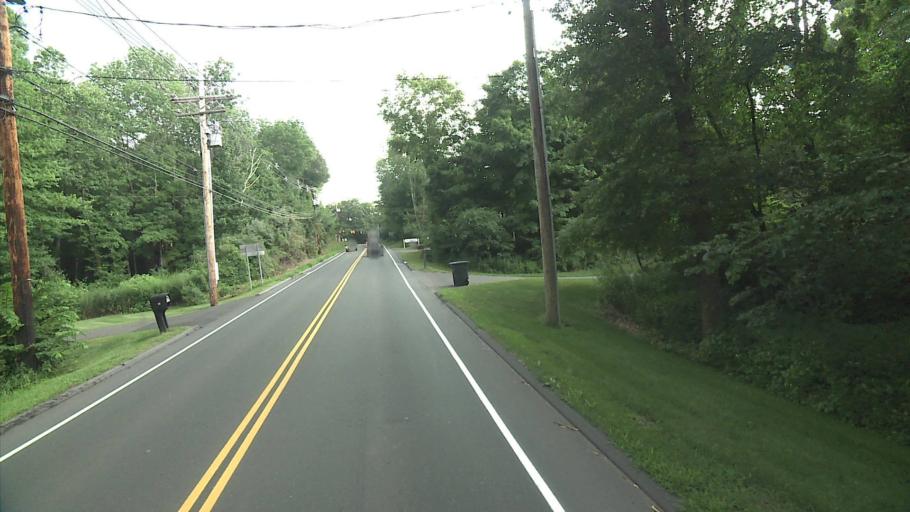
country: US
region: Connecticut
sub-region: New Haven County
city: Southbury
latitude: 41.4989
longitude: -73.2153
